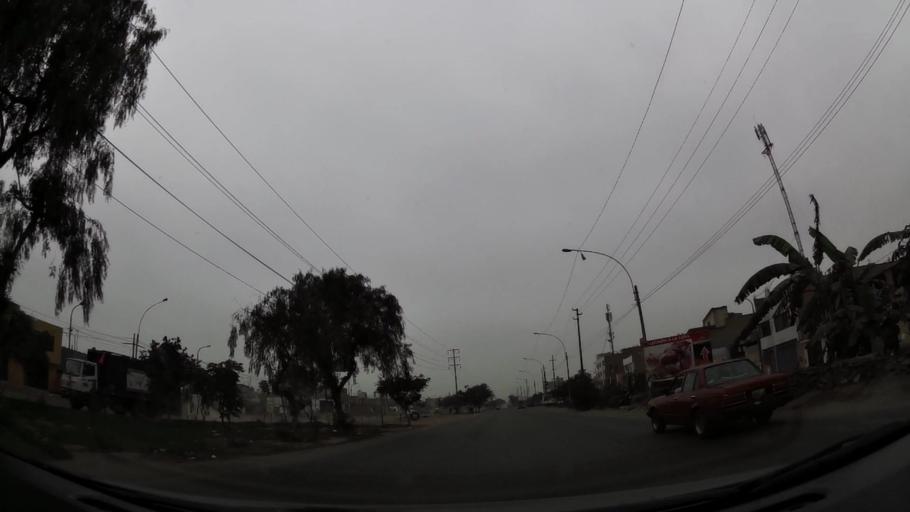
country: PE
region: Lima
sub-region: Lima
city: Urb. Santo Domingo
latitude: -11.9199
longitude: -77.0613
